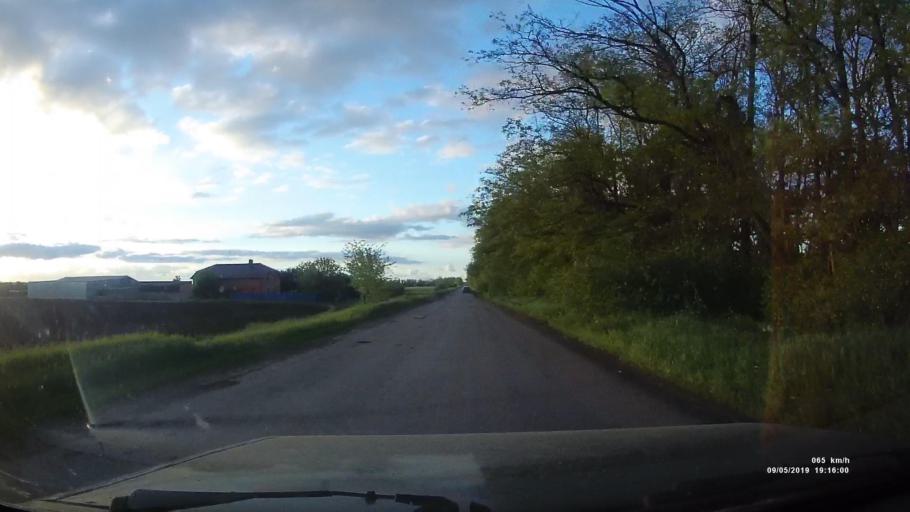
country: RU
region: Krasnodarskiy
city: Kanelovskaya
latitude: 46.7738
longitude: 39.2114
